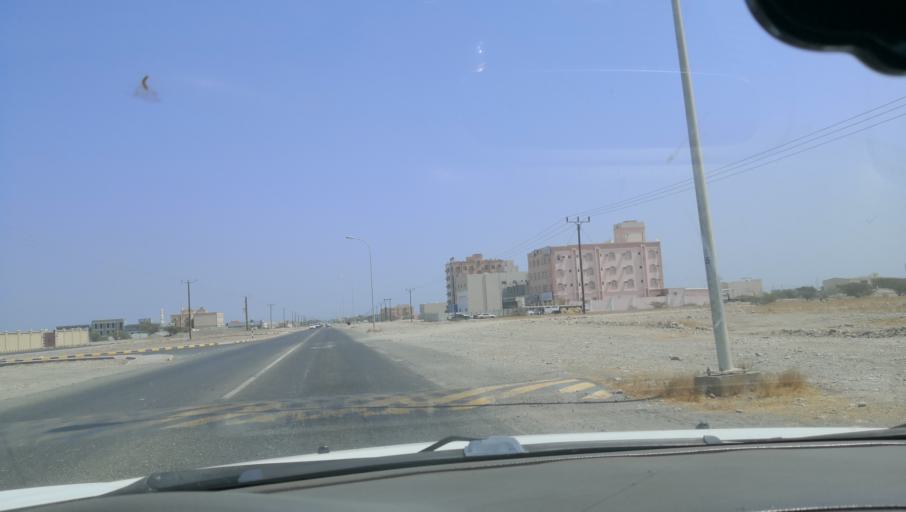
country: OM
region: Al Batinah
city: Al Khaburah
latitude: 23.9484
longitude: 57.0539
